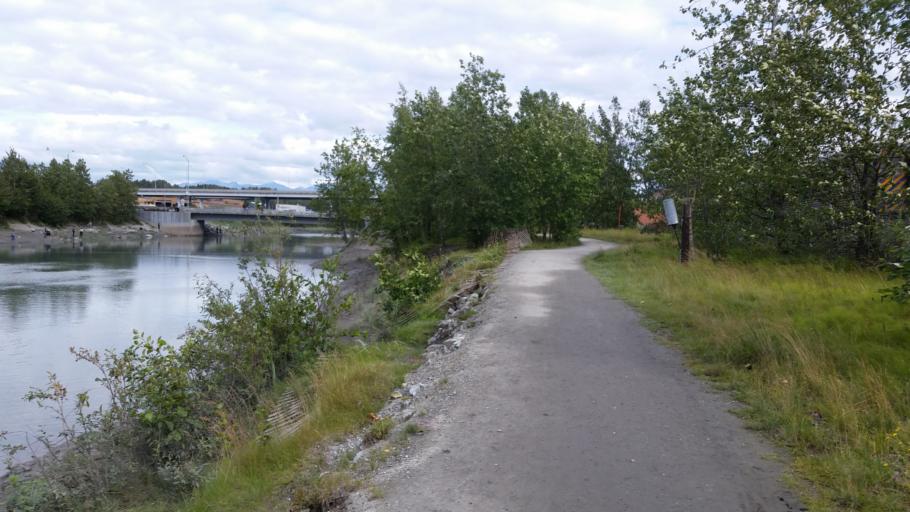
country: US
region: Alaska
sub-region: Anchorage Municipality
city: Anchorage
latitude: 61.2232
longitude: -149.8913
